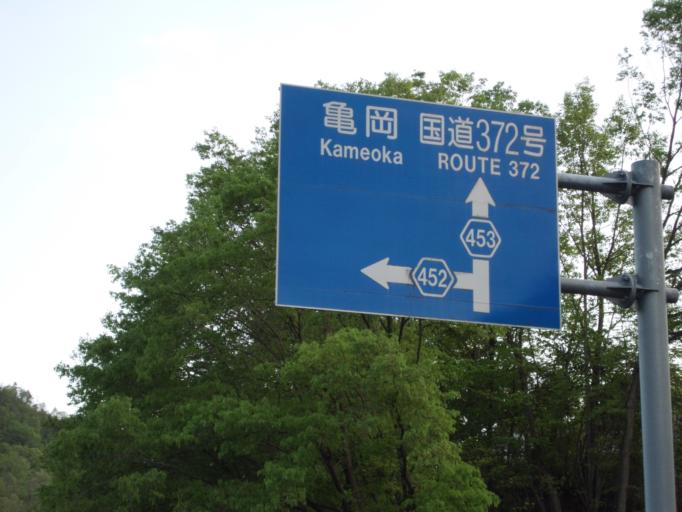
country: JP
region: Kyoto
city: Kameoka
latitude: 35.0761
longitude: 135.4381
